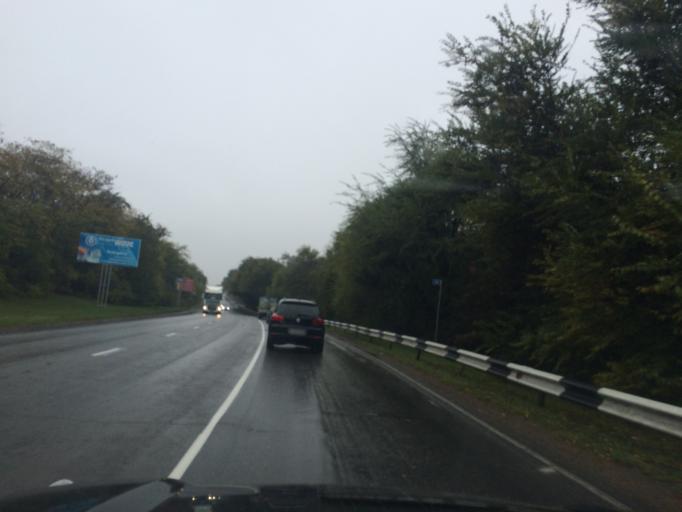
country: RU
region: Rostov
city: Azov
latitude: 47.0871
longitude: 39.4688
